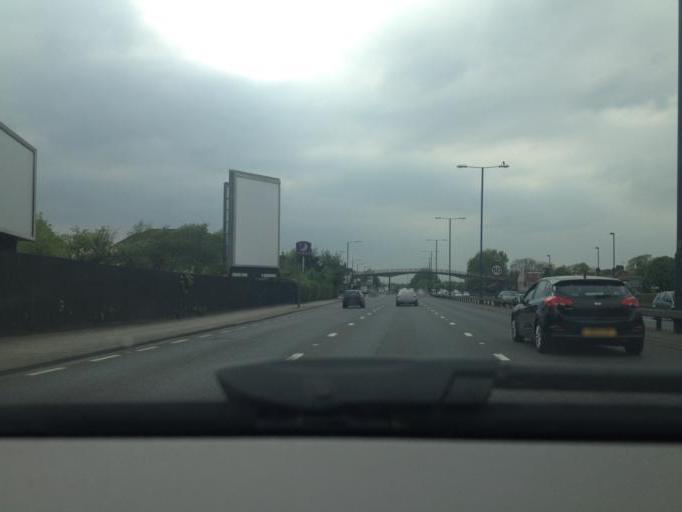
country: GB
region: England
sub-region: Greater London
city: Ealing Broadway
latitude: 51.5331
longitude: -0.3207
